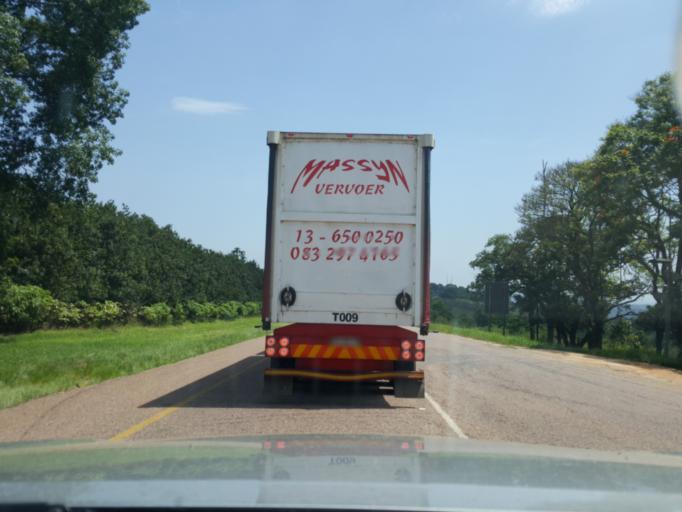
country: ZA
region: Mpumalanga
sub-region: Ehlanzeni District
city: White River
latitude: -25.1085
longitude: 31.0642
